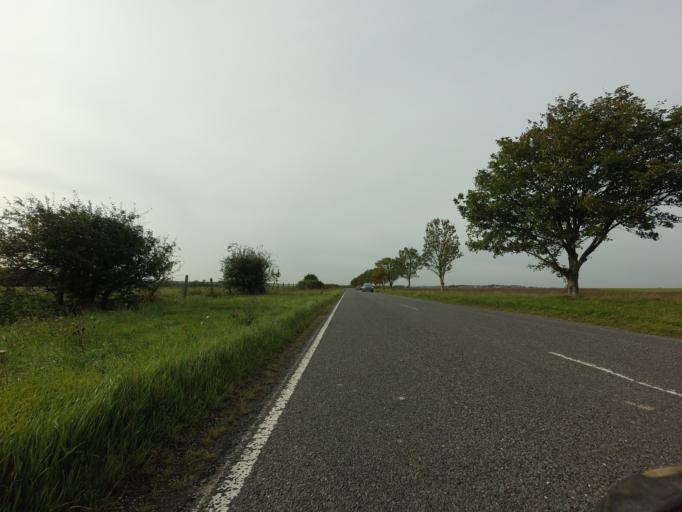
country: GB
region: England
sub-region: Cambridgeshire
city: Melbourn
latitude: 52.0784
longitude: 0.0675
